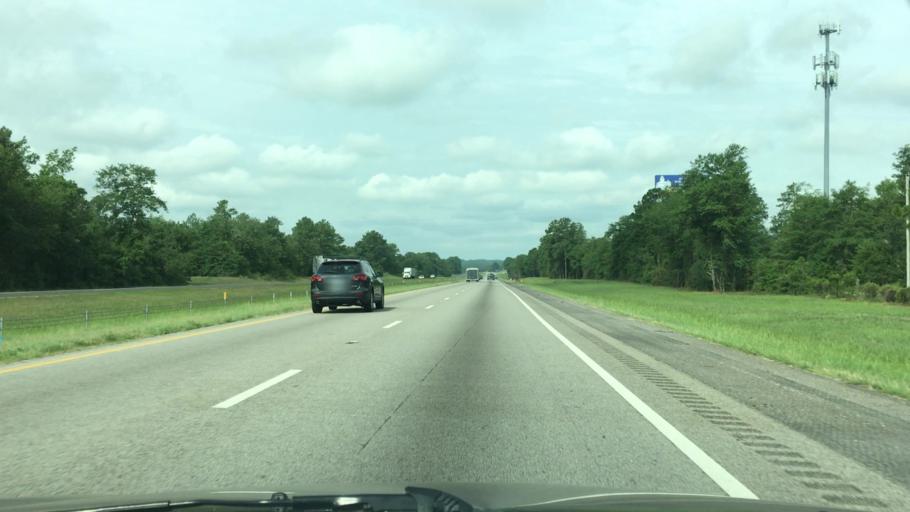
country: US
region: South Carolina
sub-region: Aiken County
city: Aiken
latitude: 33.6589
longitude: -81.6918
